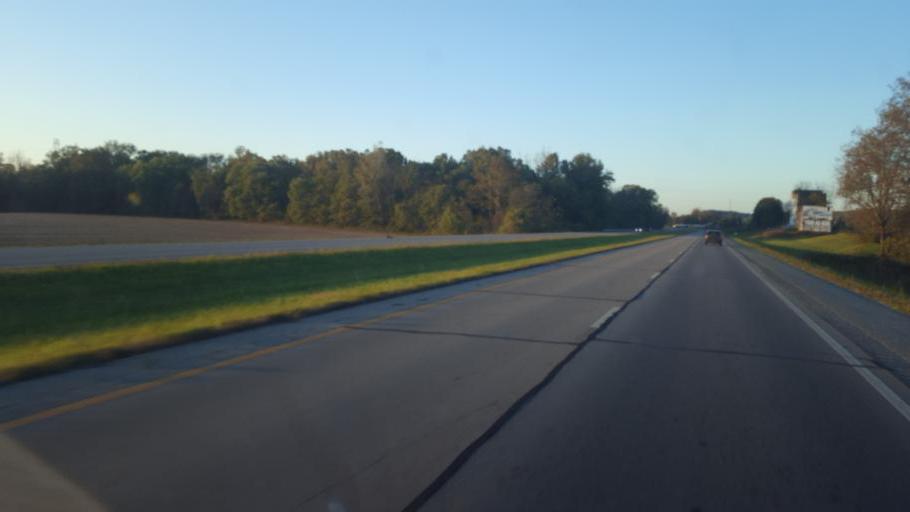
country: US
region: Ohio
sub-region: Pike County
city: Piketon
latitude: 38.9861
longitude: -83.0232
